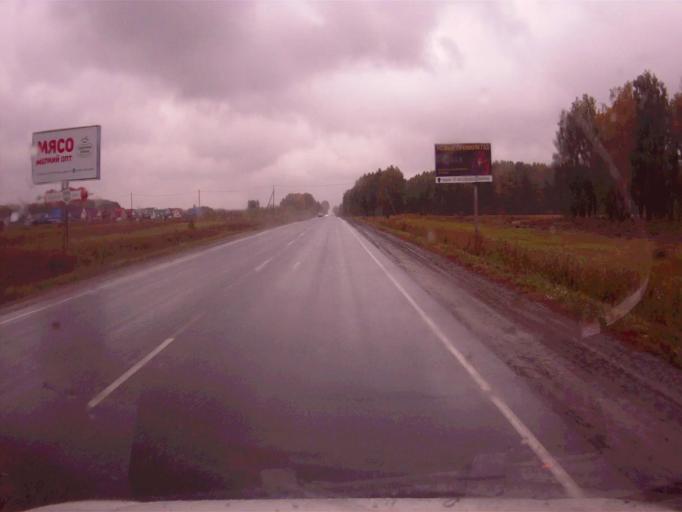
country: RU
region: Chelyabinsk
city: Argayash
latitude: 55.4205
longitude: 61.0169
